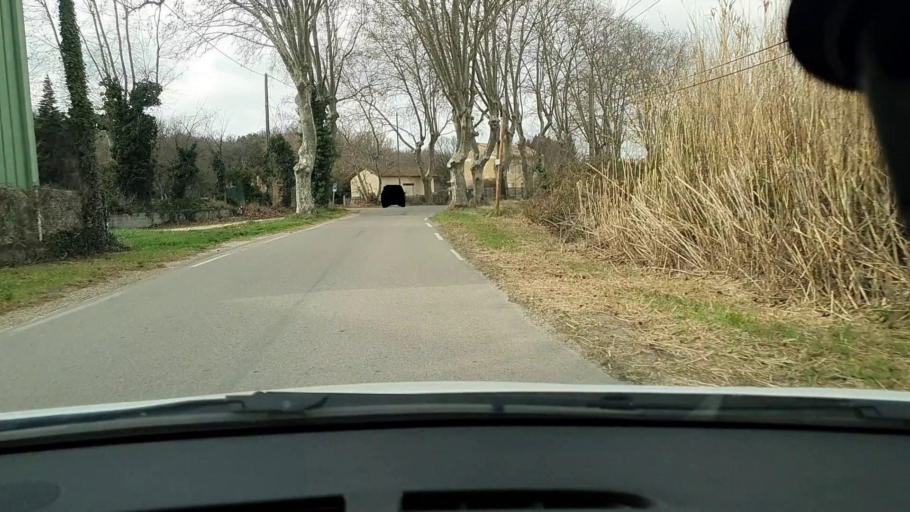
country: FR
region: Languedoc-Roussillon
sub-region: Departement du Gard
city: Meynes
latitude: 43.8716
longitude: 4.5774
